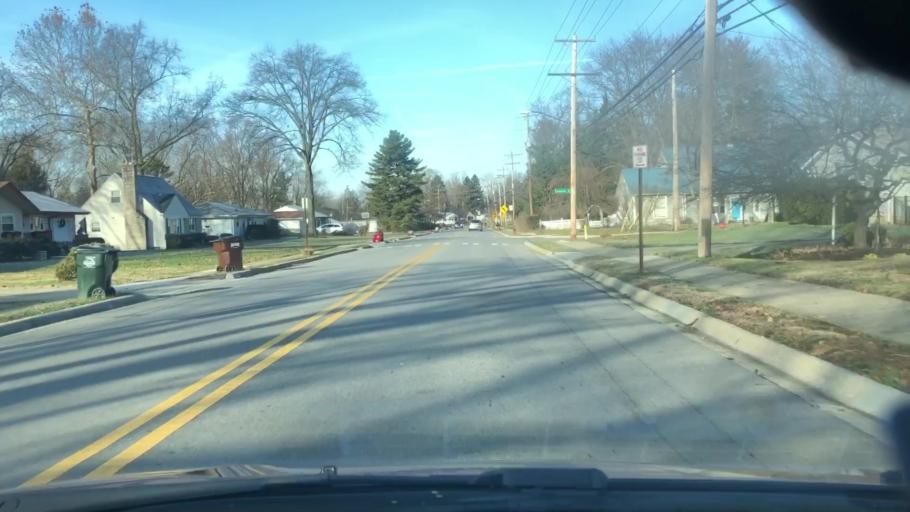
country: US
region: Ohio
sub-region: Franklin County
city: Westerville
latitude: 40.1203
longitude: -82.9187
